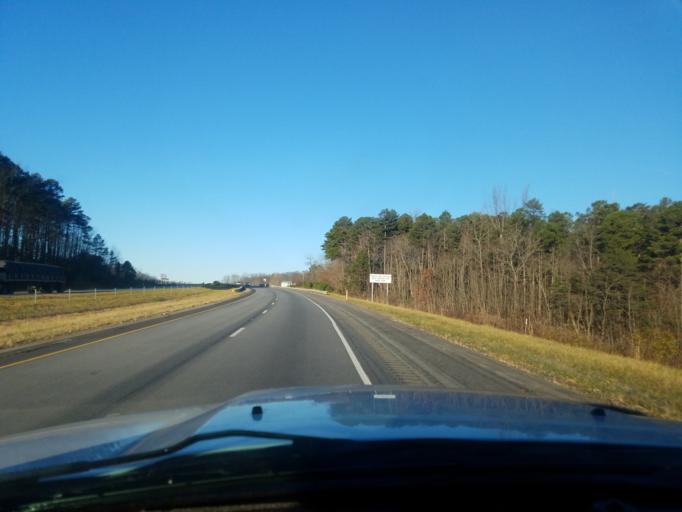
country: US
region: Indiana
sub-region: Crawford County
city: English
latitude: 38.2295
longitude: -86.6047
